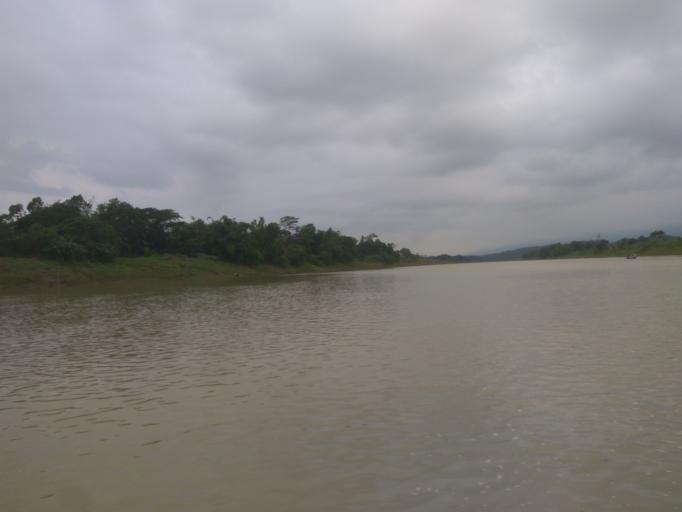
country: IN
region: Assam
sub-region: Karimganj
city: Karimganj
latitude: 24.9972
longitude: 92.3869
